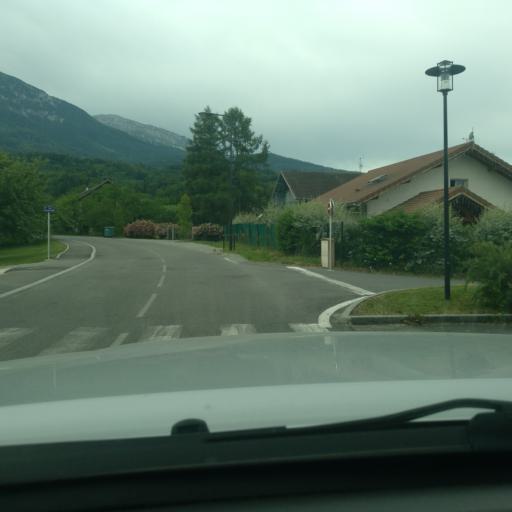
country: FR
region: Rhone-Alpes
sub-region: Departement de la Haute-Savoie
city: Amancy
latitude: 46.0618
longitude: 6.3554
